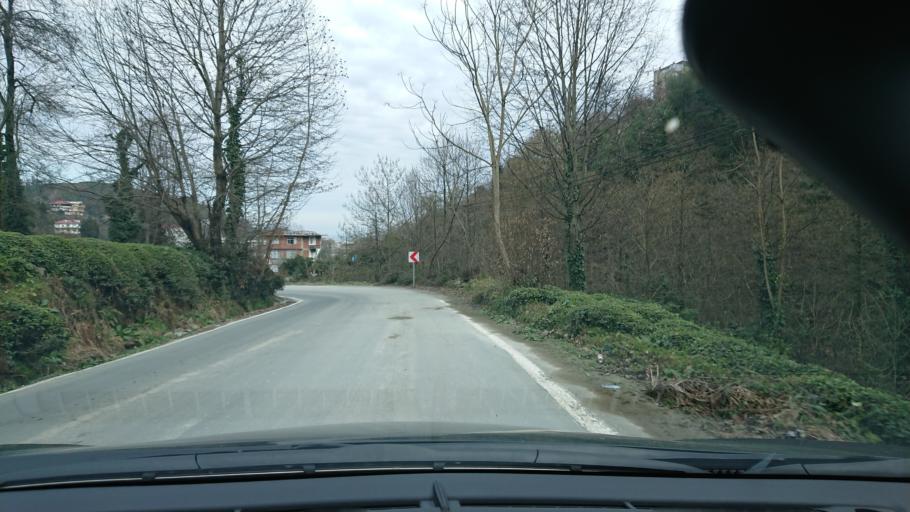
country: TR
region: Rize
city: Rize
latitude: 41.0220
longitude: 40.5026
